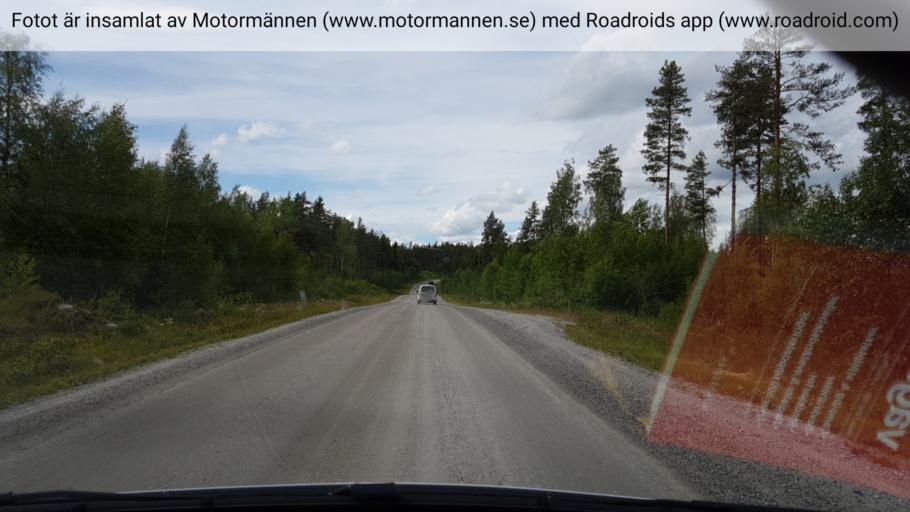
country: SE
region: Vaesternorrland
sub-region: Solleftea Kommun
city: Solleftea
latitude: 63.3130
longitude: 17.2587
